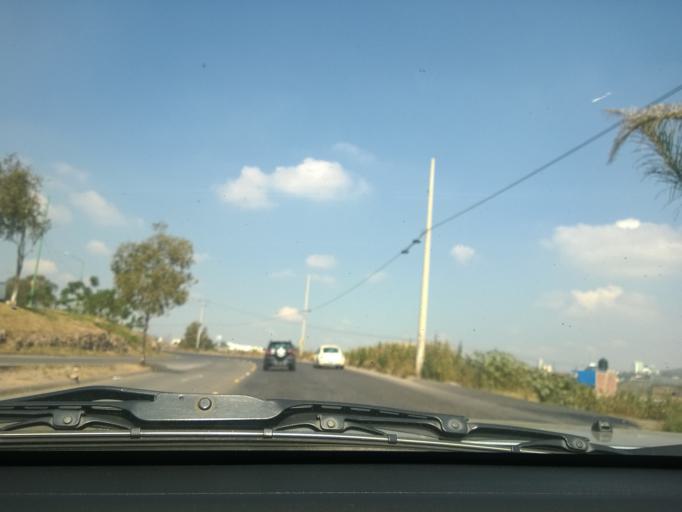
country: MX
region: Guanajuato
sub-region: Leon
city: La Ermita
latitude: 21.1345
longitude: -101.7151
